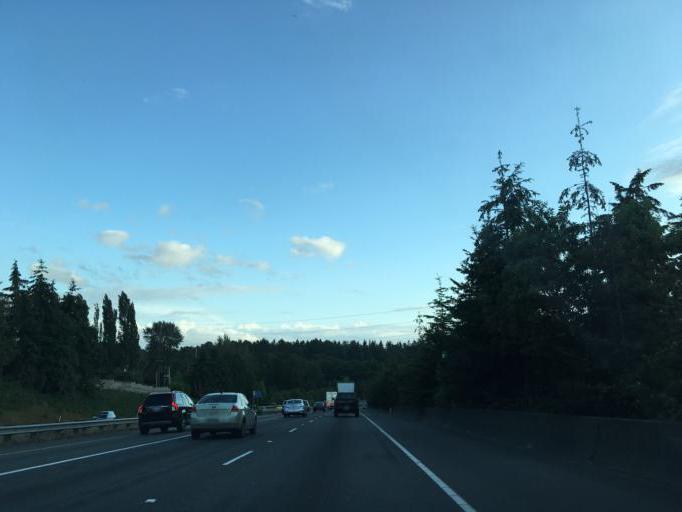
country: US
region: Washington
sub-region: King County
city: Newport
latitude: 47.5705
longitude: -122.1782
